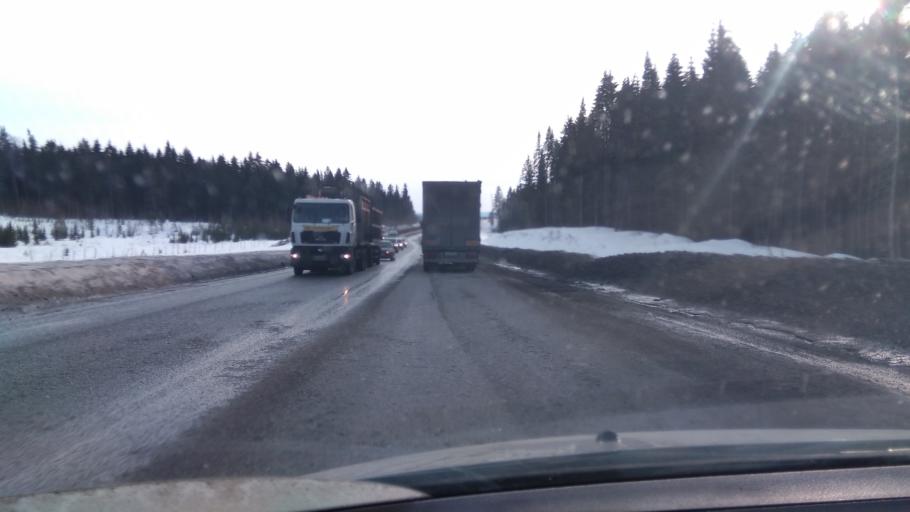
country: RU
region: Perm
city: Ferma
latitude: 57.9472
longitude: 56.3849
